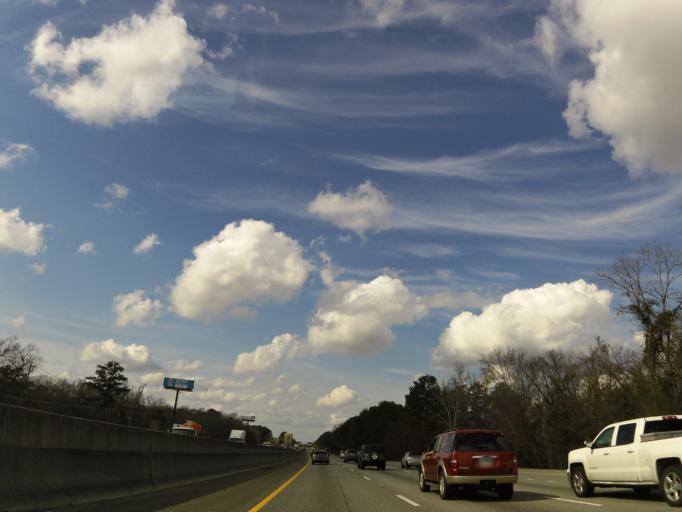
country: US
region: South Carolina
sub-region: Berkeley County
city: Hanahan
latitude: 32.9444
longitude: -80.0537
